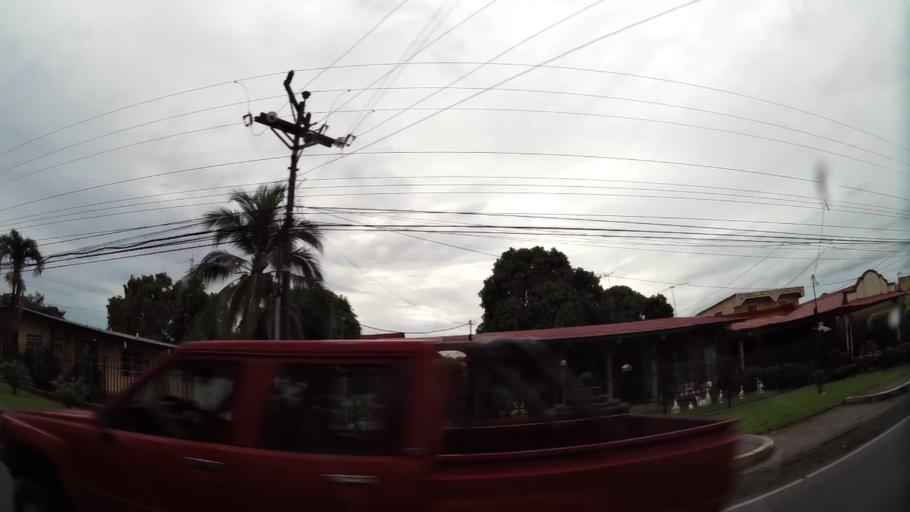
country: PA
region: Veraguas
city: Santiago de Veraguas
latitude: 8.1086
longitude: -80.9771
